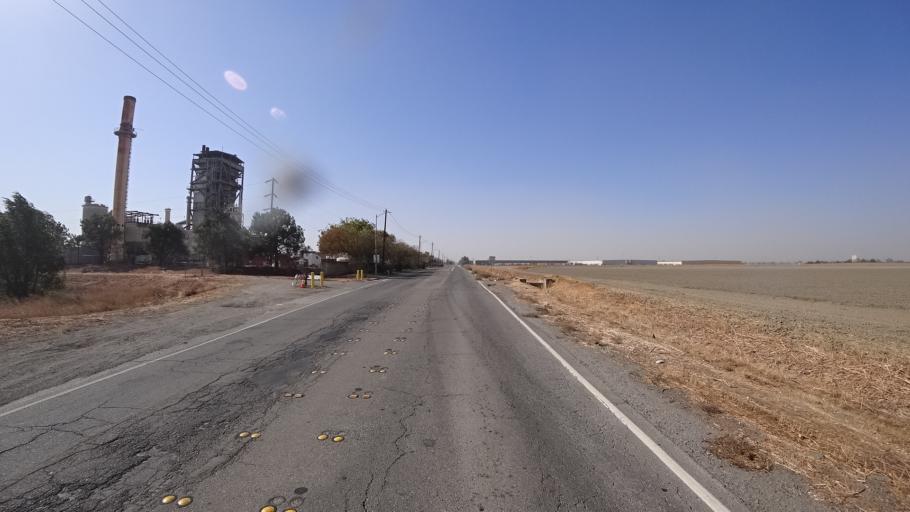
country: US
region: California
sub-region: Yolo County
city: Woodland
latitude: 38.6917
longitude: -121.7355
